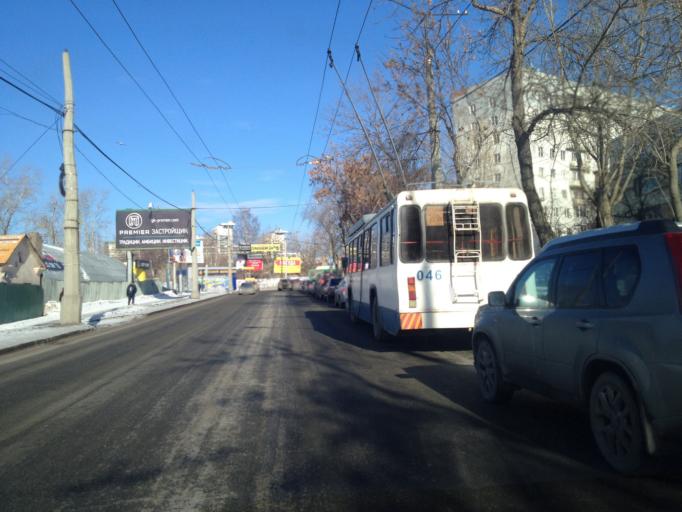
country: RU
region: Sverdlovsk
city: Yekaterinburg
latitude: 56.8237
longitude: 60.5685
